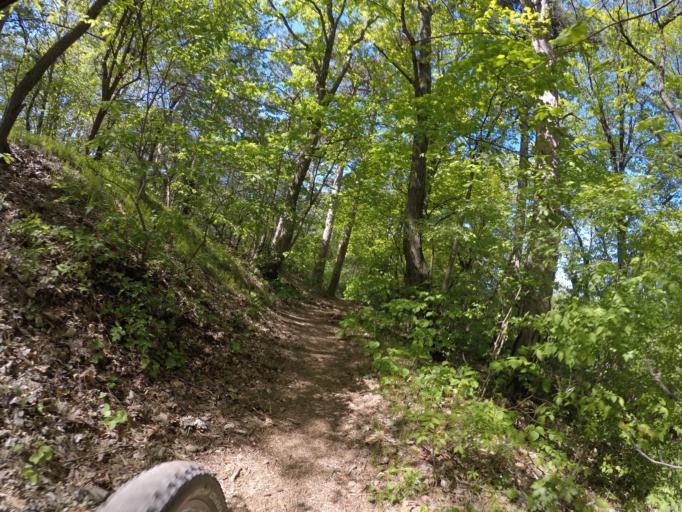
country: AT
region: Lower Austria
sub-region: Politischer Bezirk Modling
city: Modling
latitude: 48.0684
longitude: 16.2816
